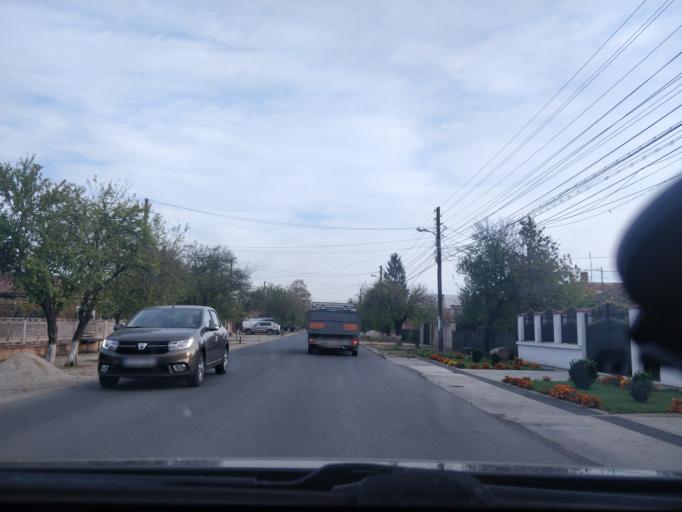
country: RO
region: Giurgiu
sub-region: Comuna Bolintin Vale
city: Malu Spart
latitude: 44.4372
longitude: 25.7205
